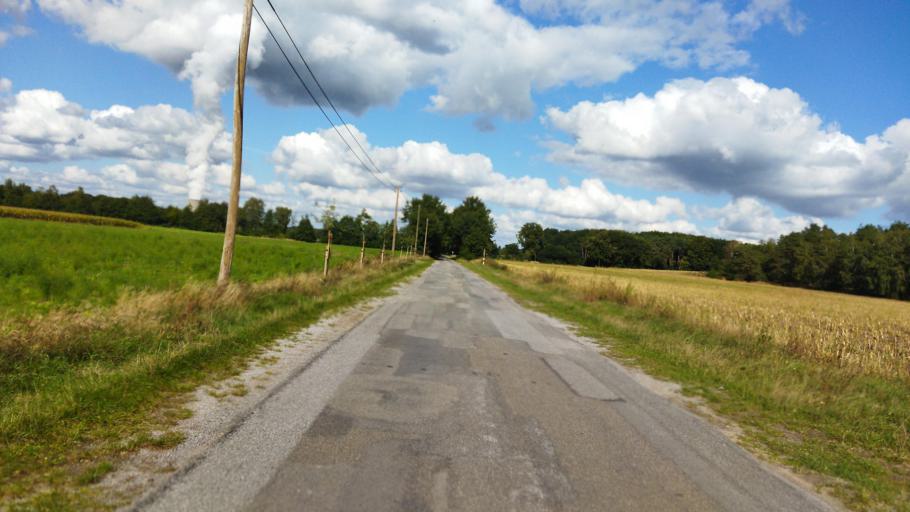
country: DE
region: Lower Saxony
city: Emsburen
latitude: 52.4359
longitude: 7.3398
